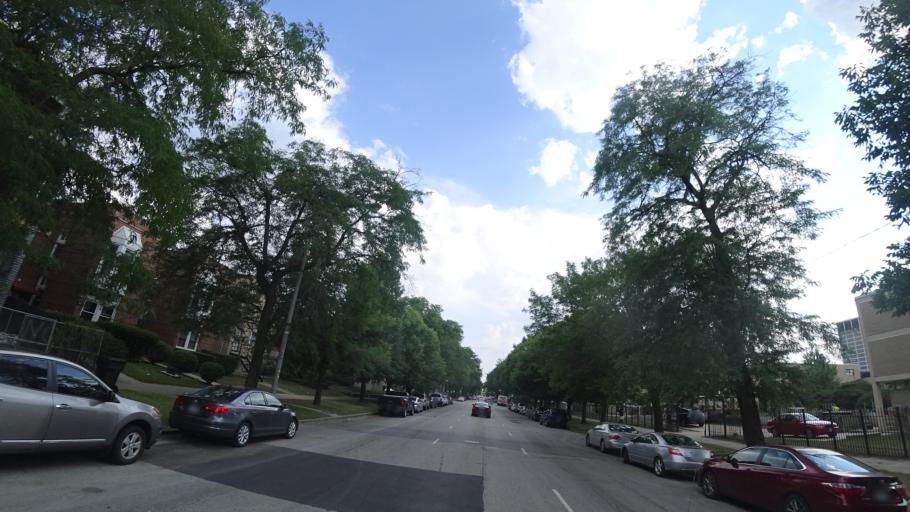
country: US
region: Illinois
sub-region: Cook County
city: Chicago
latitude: 41.8339
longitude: -87.6233
